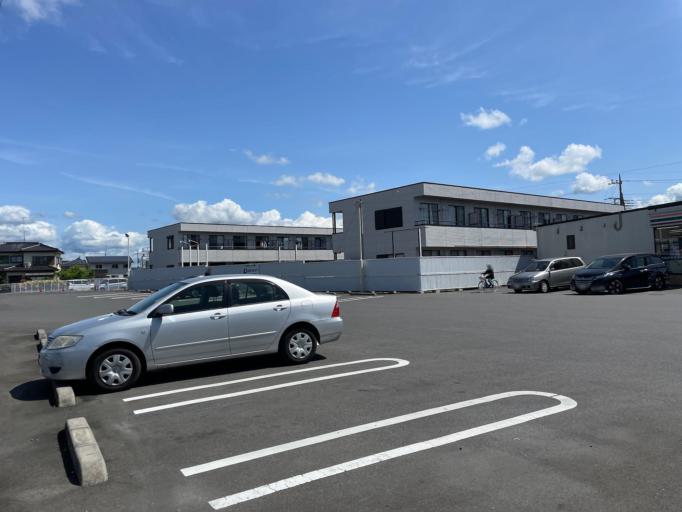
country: JP
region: Tochigi
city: Sano
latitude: 36.3142
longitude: 139.5354
